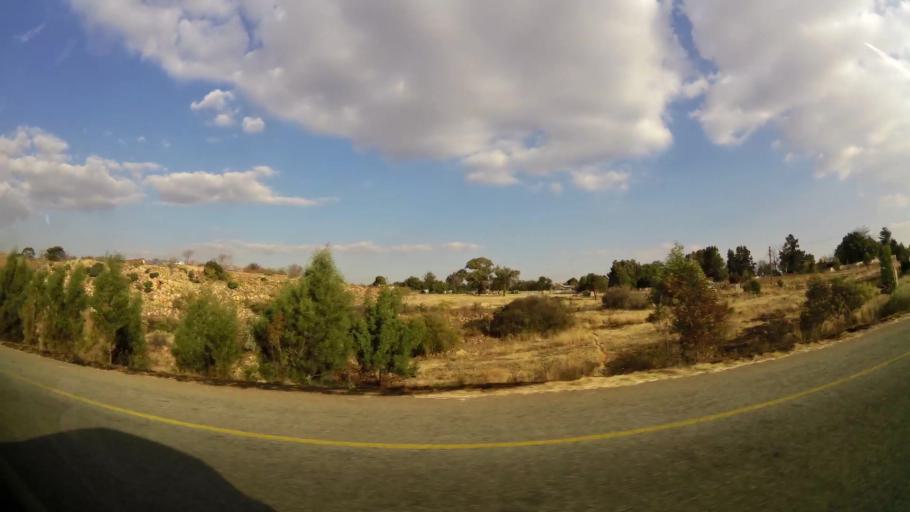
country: ZA
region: Gauteng
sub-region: West Rand District Municipality
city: Krugersdorp
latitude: -26.0854
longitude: 27.7397
